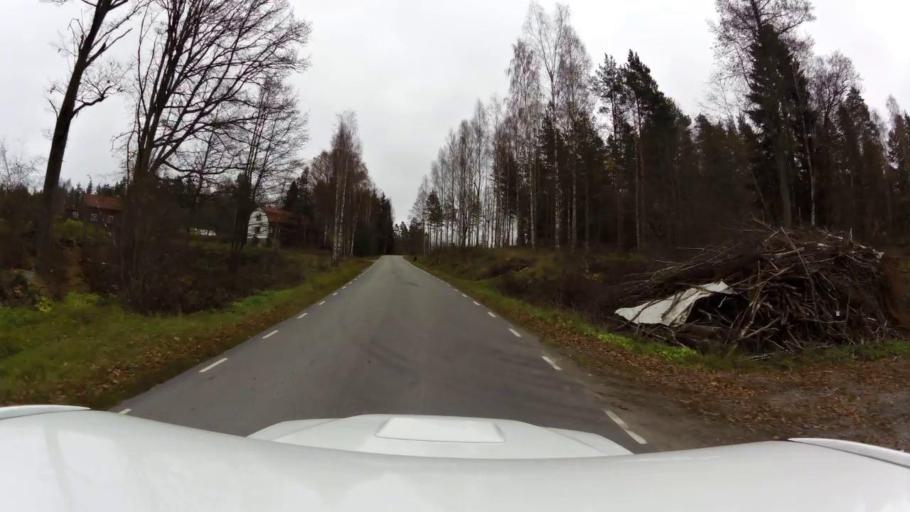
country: SE
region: OEstergoetland
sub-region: Kinda Kommun
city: Rimforsa
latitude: 58.1418
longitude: 15.6533
